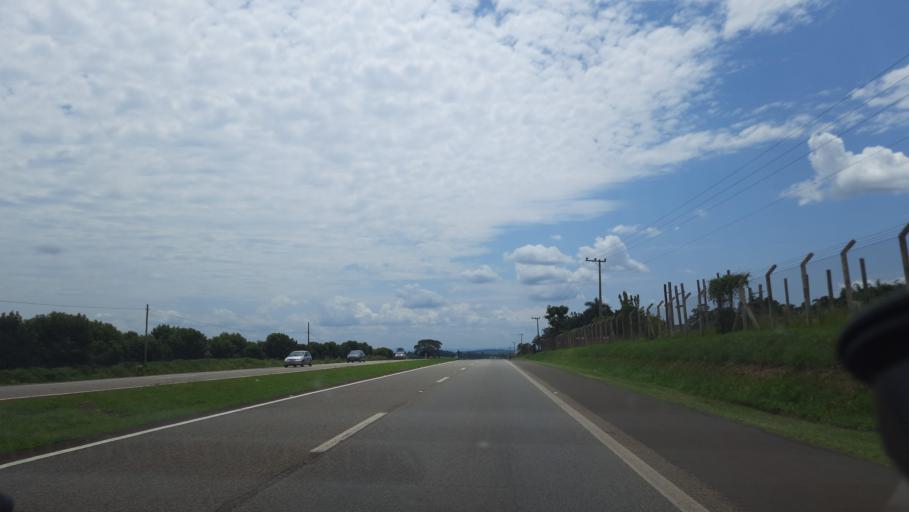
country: BR
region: Sao Paulo
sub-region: Casa Branca
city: Casa Branca
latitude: -21.7444
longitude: -47.0723
